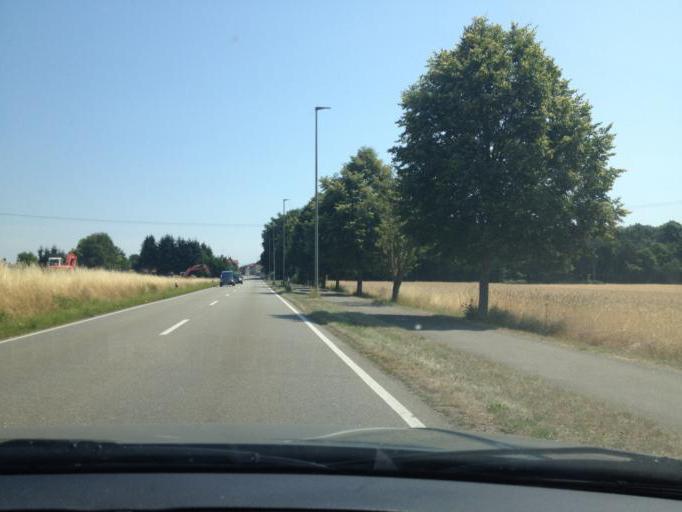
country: DE
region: Rheinland-Pfalz
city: Hutschenhausen
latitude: 49.4223
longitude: 7.4920
